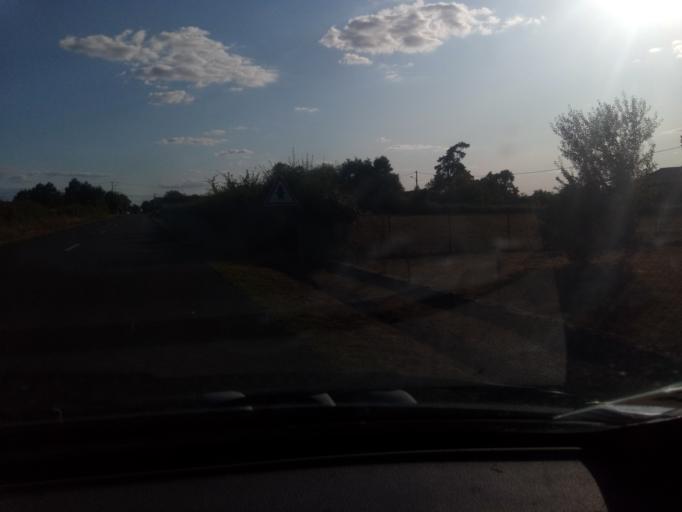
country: FR
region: Poitou-Charentes
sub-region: Departement de la Vienne
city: Availles-Limouzine
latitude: 46.1534
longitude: 0.7205
